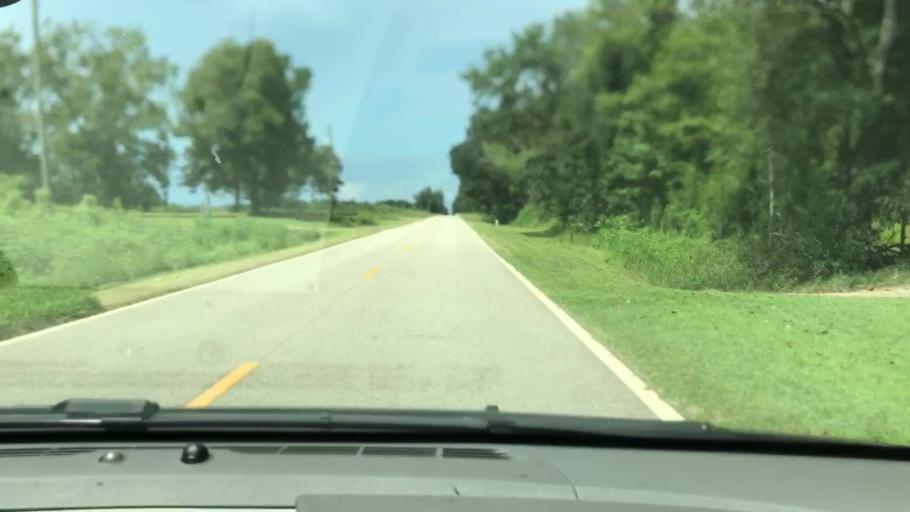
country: US
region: Georgia
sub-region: Seminole County
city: Donalsonville
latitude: 31.1284
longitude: -84.9954
